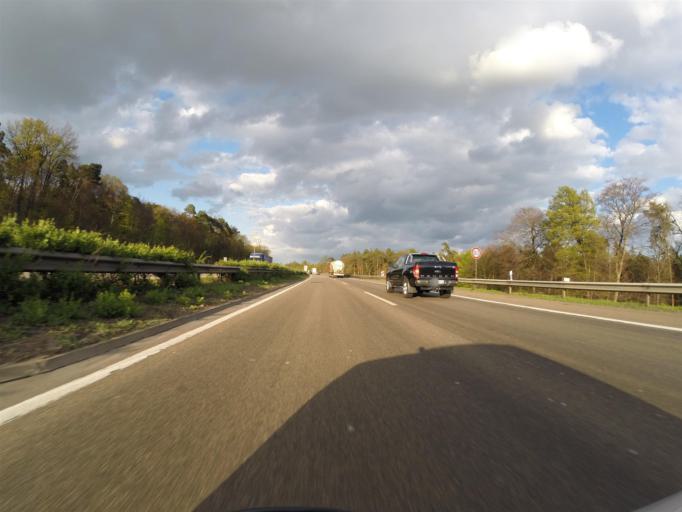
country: DE
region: Rheinland-Pfalz
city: Otterbach
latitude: 49.4495
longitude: 7.7243
